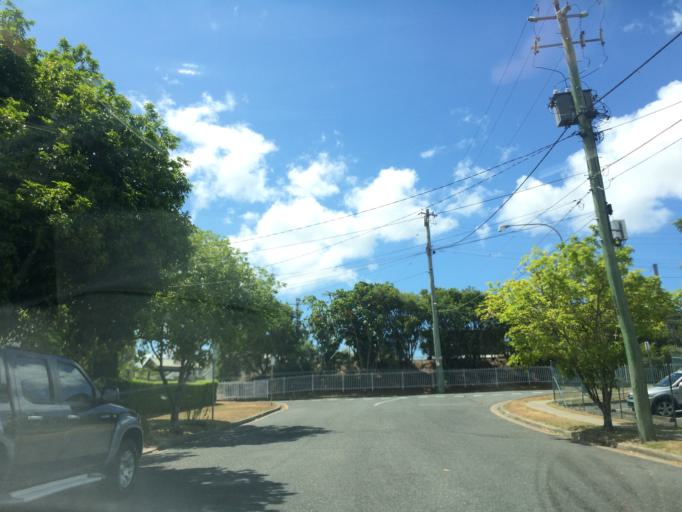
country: AU
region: Queensland
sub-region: Brisbane
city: Seven Hills
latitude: -27.4825
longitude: 153.0619
